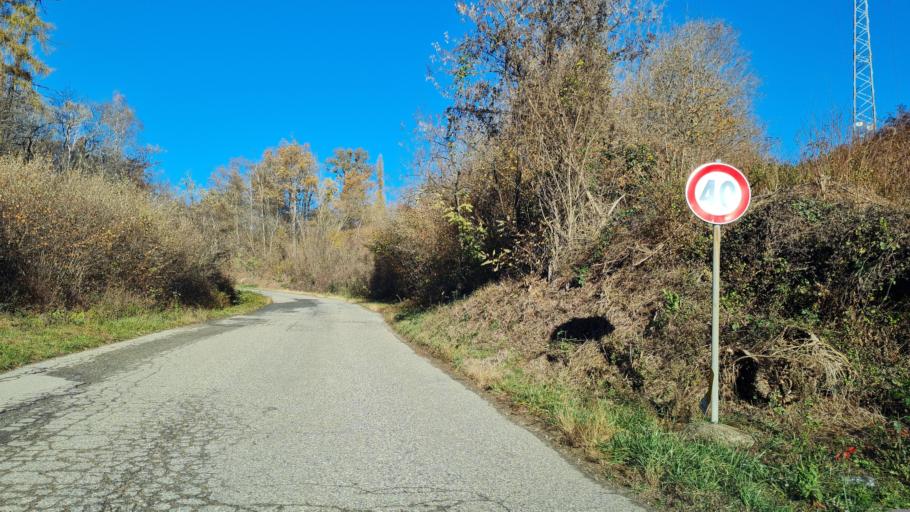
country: IT
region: Piedmont
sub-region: Provincia di Biella
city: Curino
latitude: 45.6090
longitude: 8.2421
